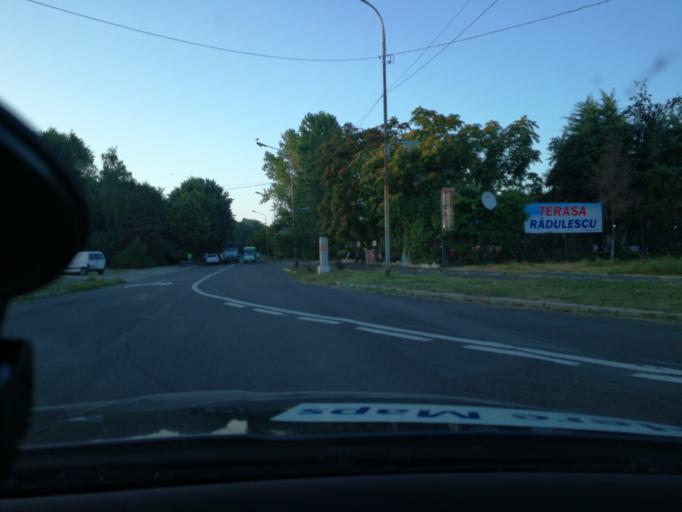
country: RO
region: Constanta
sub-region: Comuna Douazeci si Trei August
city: Douazeci si Trei August
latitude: 43.8731
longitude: 28.5999
